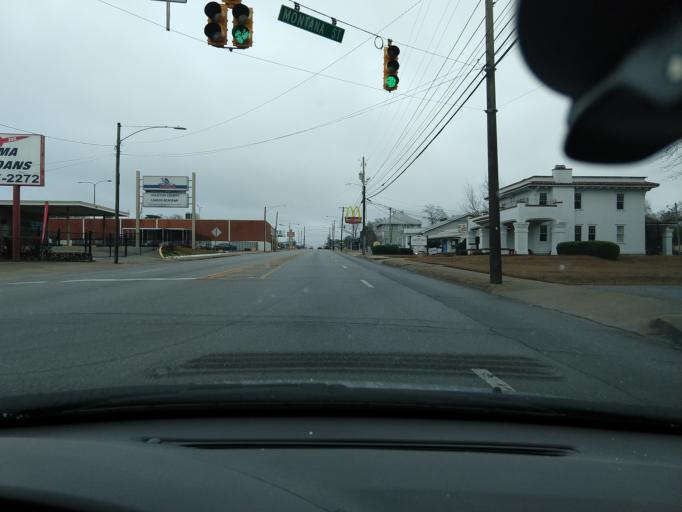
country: US
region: Alabama
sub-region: Houston County
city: Dothan
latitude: 31.2257
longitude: -85.4025
